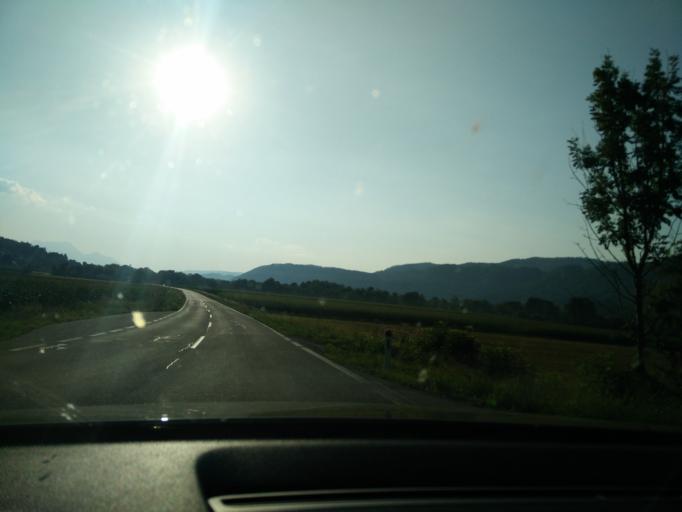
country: AT
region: Carinthia
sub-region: Politischer Bezirk Klagenfurt Land
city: Ferlach
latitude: 46.5398
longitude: 14.3654
